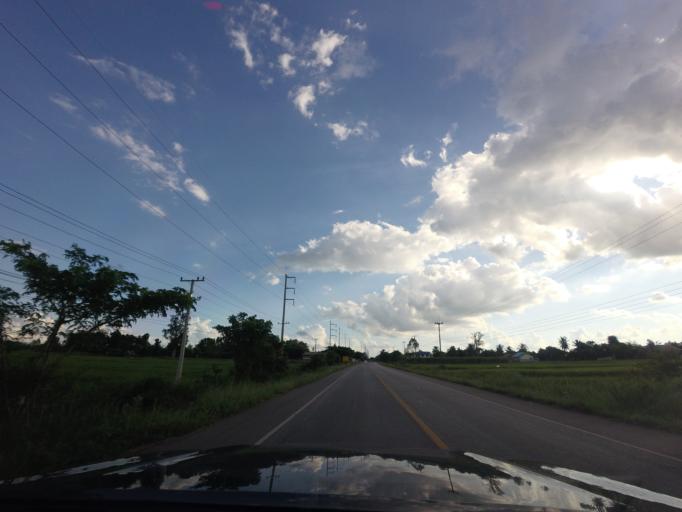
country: TH
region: Changwat Udon Thani
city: Thung Fon
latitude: 17.4593
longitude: 103.1887
